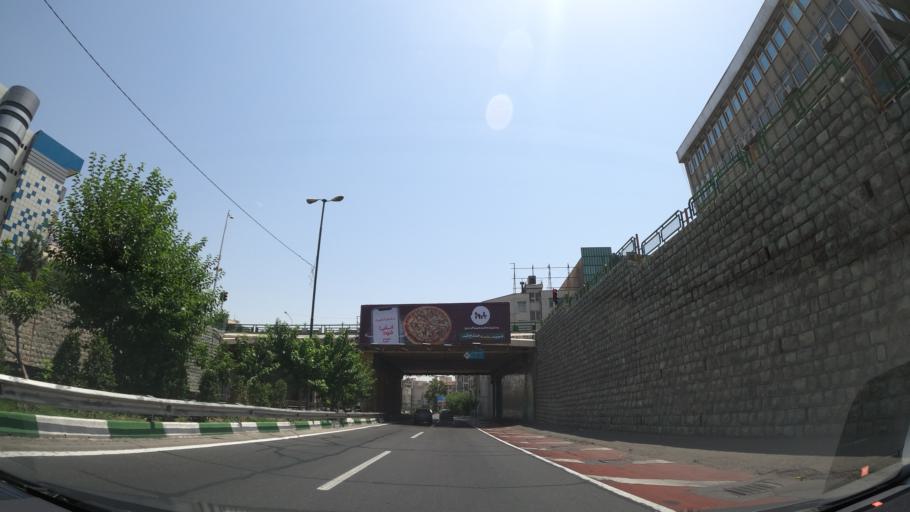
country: IR
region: Tehran
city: Tehran
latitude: 35.7245
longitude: 51.4247
